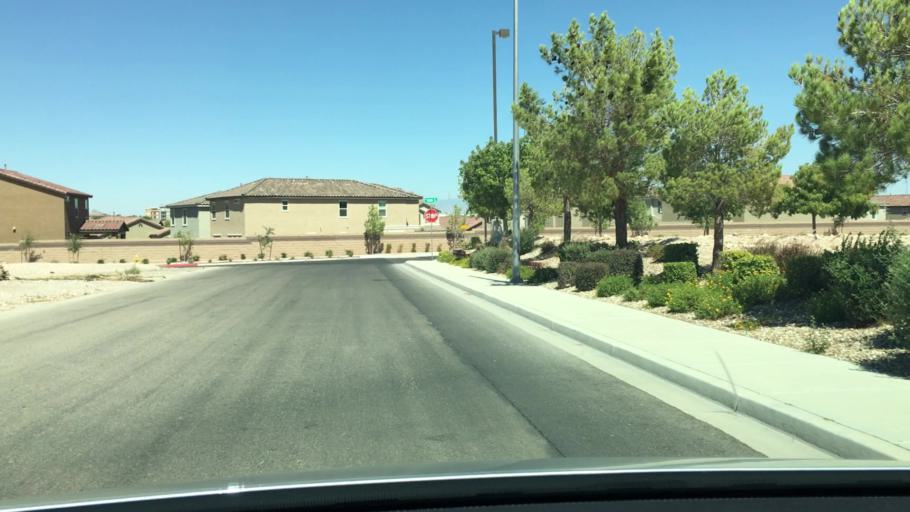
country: US
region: Nevada
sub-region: Clark County
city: Summerlin South
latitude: 36.0753
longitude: -115.2931
